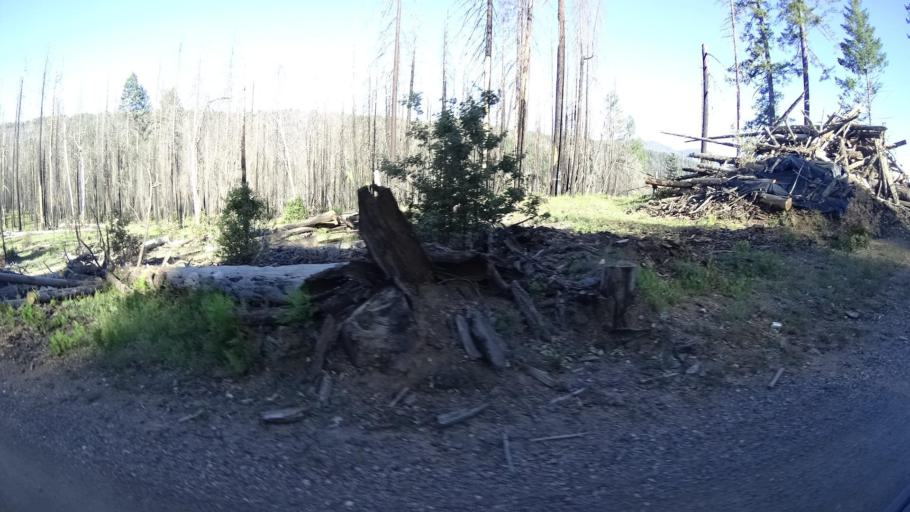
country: US
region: California
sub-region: Lake County
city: Upper Lake
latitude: 39.3708
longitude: -122.9921
